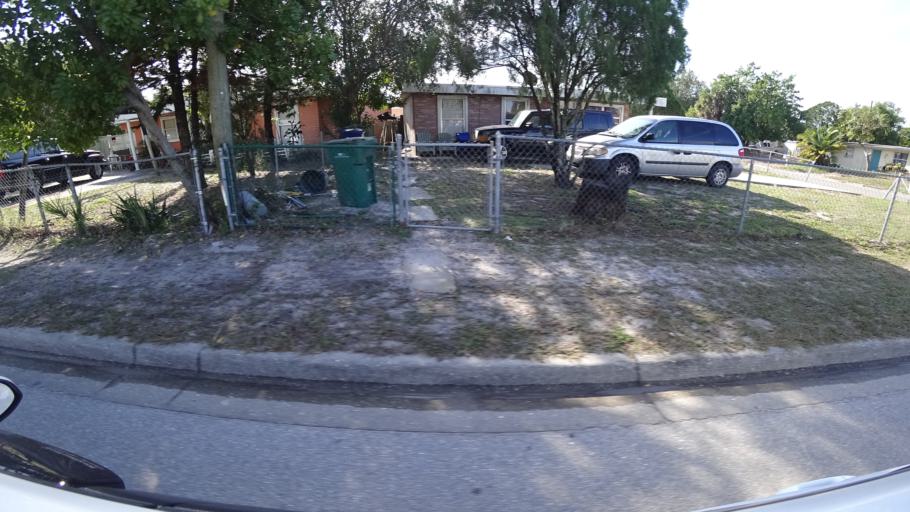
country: US
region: Florida
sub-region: Manatee County
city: Whitfield
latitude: 27.4349
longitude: -82.5634
